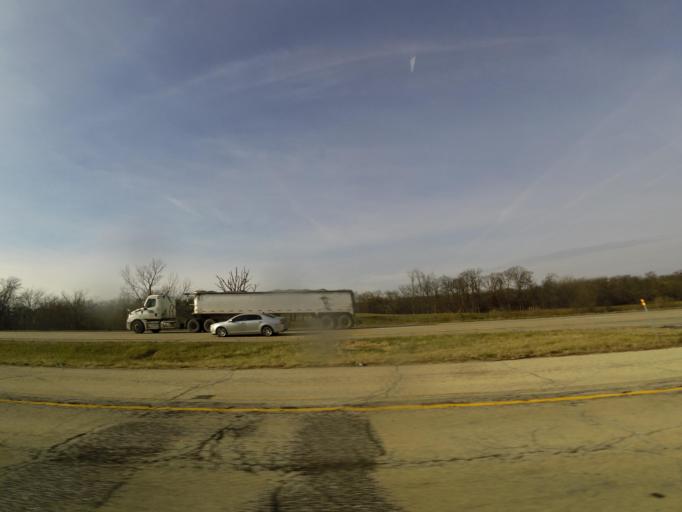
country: US
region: Illinois
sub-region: De Witt County
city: Clinton
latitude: 40.0951
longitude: -88.9655
